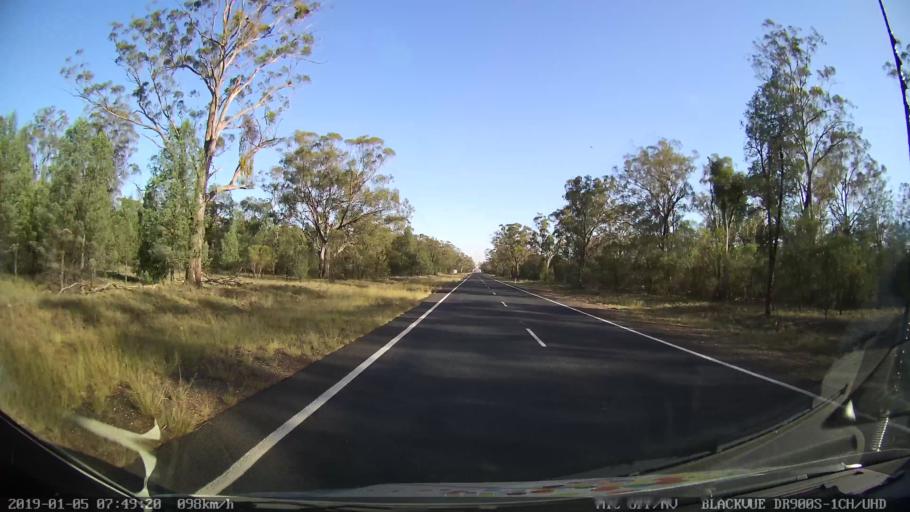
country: AU
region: New South Wales
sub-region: Gilgandra
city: Gilgandra
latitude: -31.8034
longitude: 148.6364
